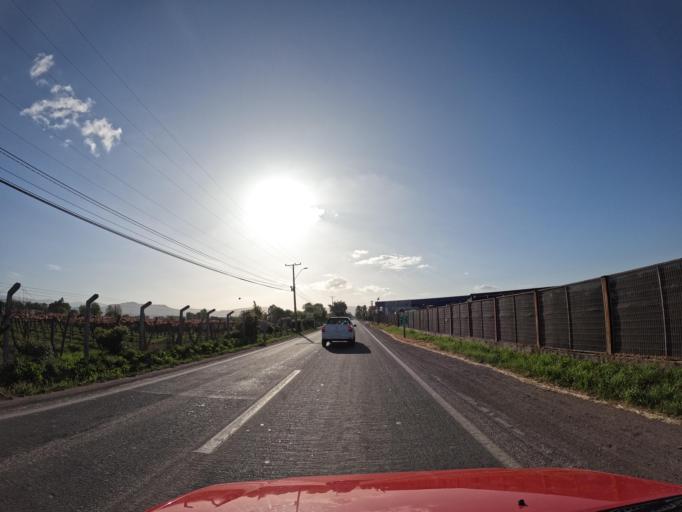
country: CL
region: O'Higgins
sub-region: Provincia de Colchagua
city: Santa Cruz
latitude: -34.6515
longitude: -71.3480
